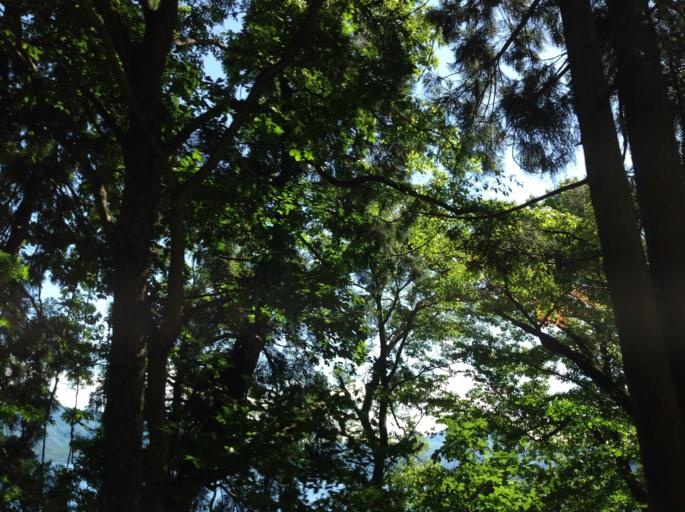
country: JP
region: Akita
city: Kakunodatemachi
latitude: 39.7027
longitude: 140.6444
